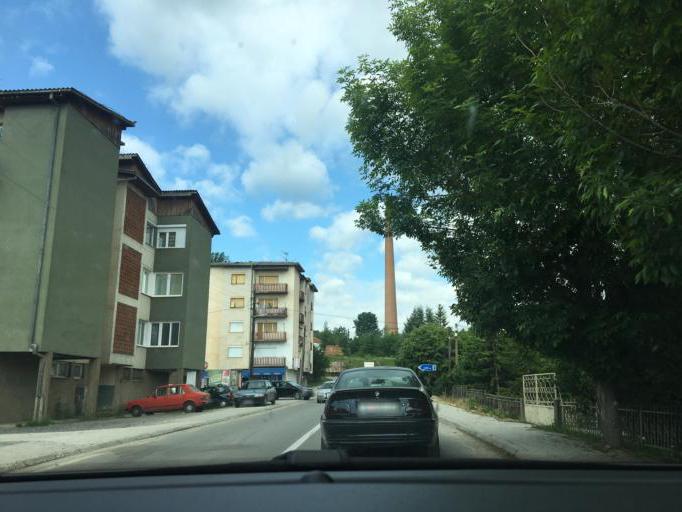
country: MK
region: Resen
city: Resen
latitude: 41.0852
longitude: 21.0099
